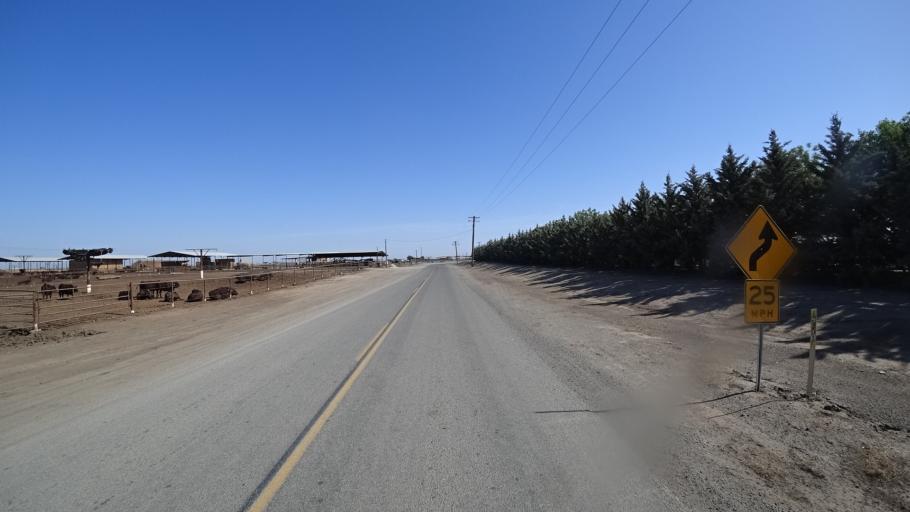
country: US
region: California
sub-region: Kings County
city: Corcoran
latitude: 36.1796
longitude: -119.5649
